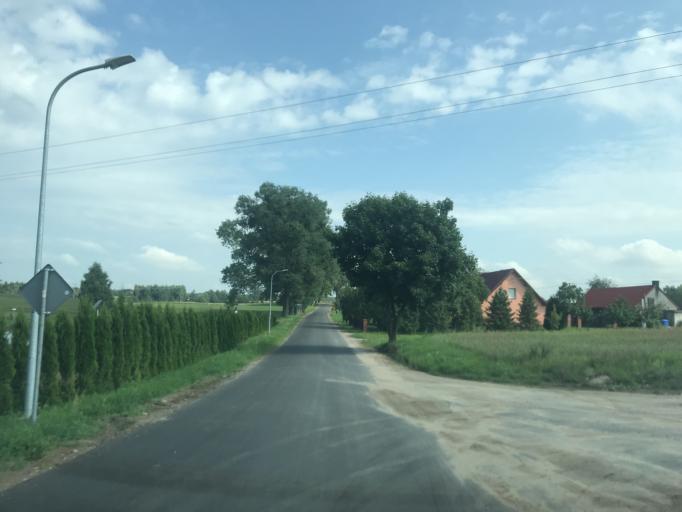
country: PL
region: Kujawsko-Pomorskie
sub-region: Powiat brodnicki
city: Brodnica
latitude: 53.3680
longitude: 19.4562
